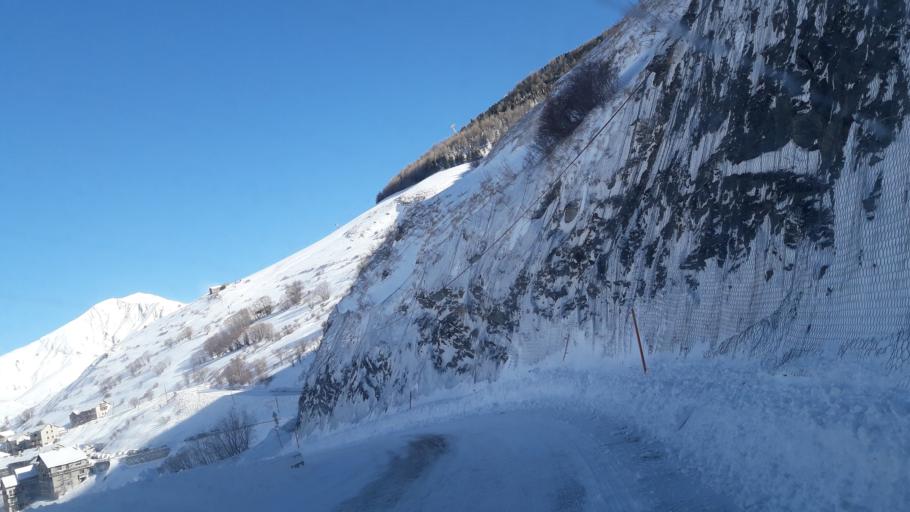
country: FR
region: Rhone-Alpes
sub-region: Departement de l'Isere
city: Mont-de-Lans
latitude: 45.0507
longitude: 6.2891
